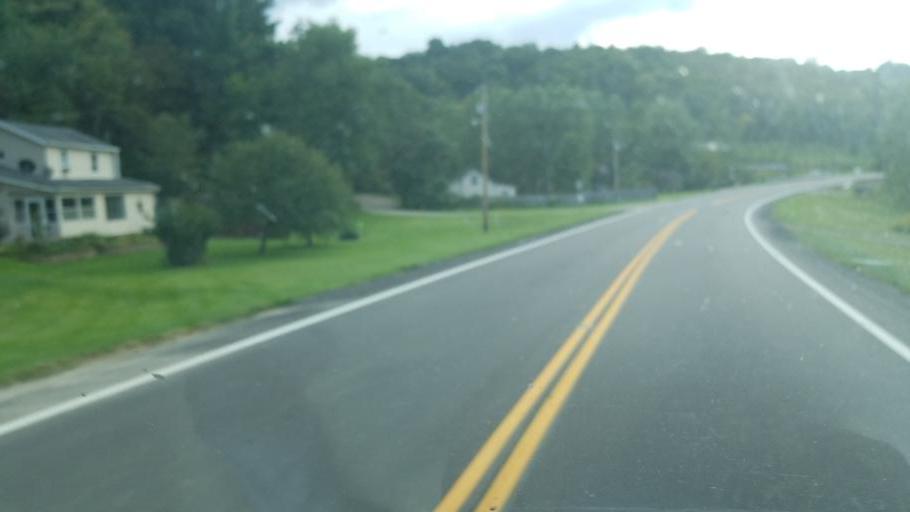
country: US
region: Ohio
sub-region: Knox County
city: Oak Hill
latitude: 40.4582
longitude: -82.1692
